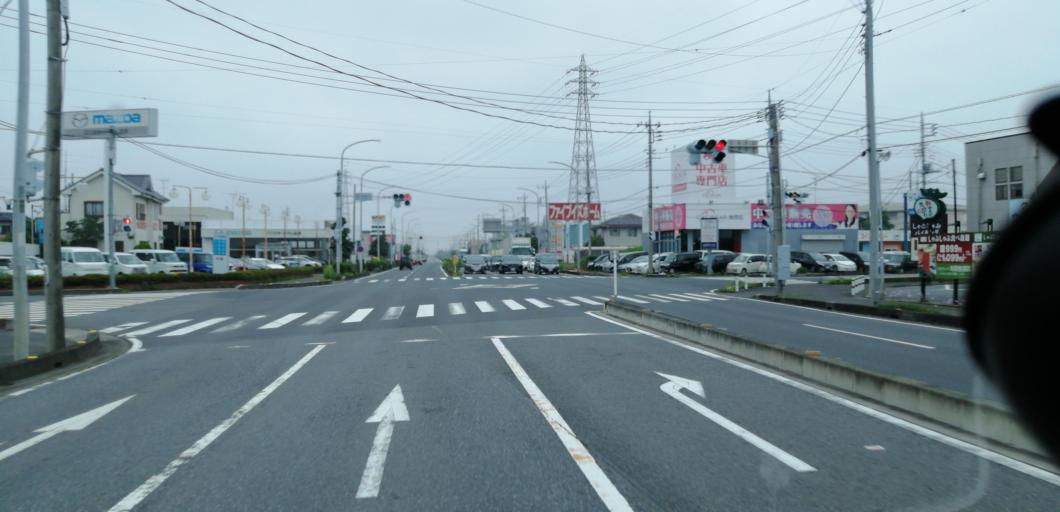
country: JP
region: Saitama
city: Kazo
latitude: 36.1332
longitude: 139.6021
